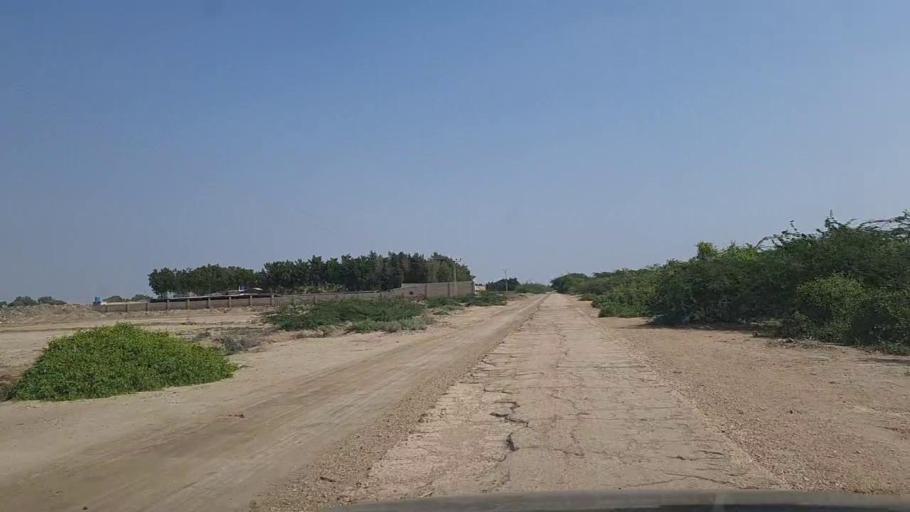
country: PK
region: Sindh
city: Gharo
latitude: 24.7413
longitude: 67.6615
